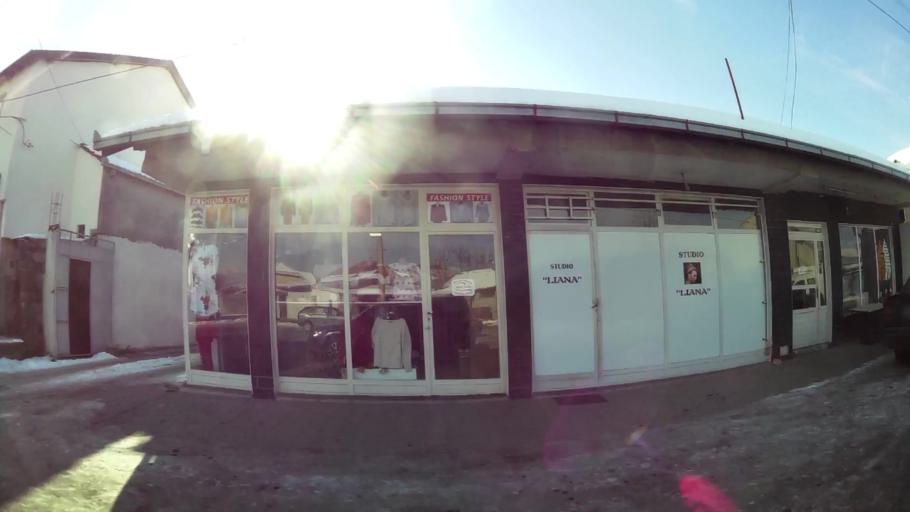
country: MK
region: Saraj
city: Saraj
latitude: 42.0004
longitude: 21.3259
